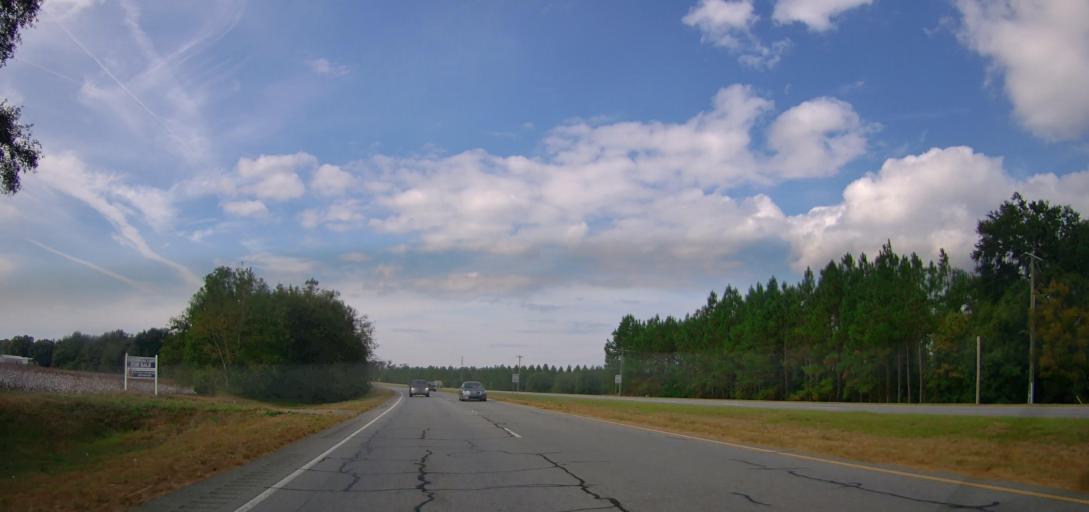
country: US
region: Georgia
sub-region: Mitchell County
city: Camilla
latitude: 31.2140
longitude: -84.1808
